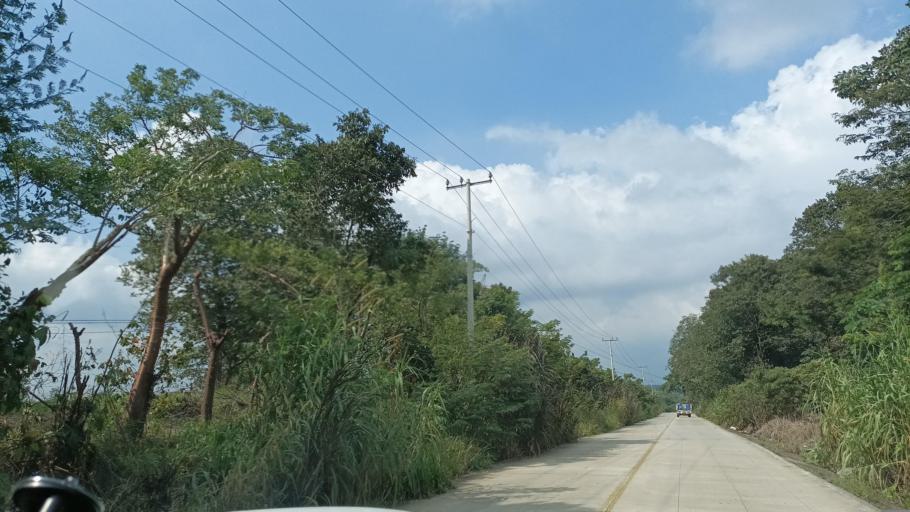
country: MX
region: Veracruz
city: Las Choapas
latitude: 17.7914
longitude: -94.1096
